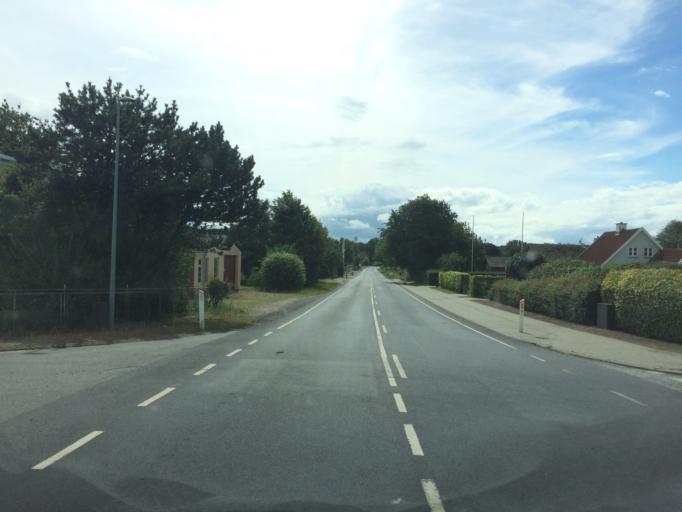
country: DK
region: South Denmark
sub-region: Faaborg-Midtfyn Kommune
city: Faaborg
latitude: 55.1999
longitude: 10.2503
